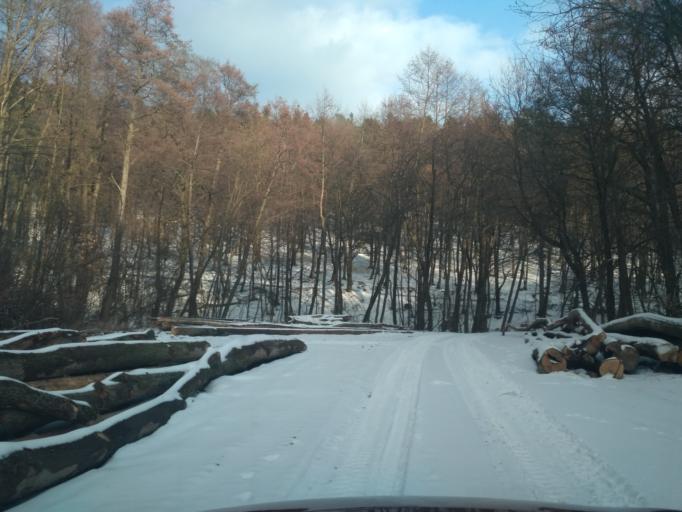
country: SK
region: Kosicky
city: Kosice
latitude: 48.7481
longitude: 21.1505
